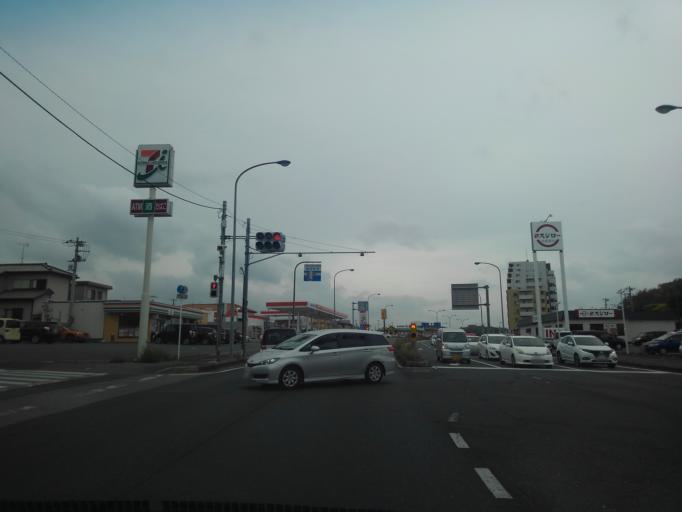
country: JP
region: Chiba
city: Kisarazu
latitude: 35.3818
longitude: 139.9424
